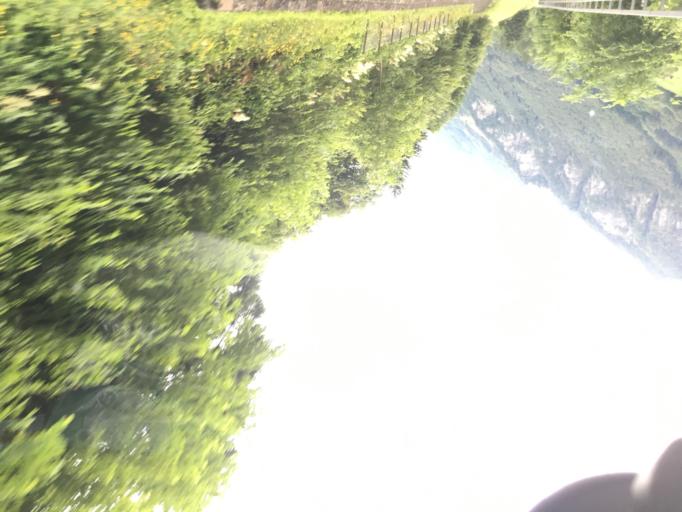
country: CH
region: Obwalden
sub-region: Obwalden
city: Engelberg
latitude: 46.8565
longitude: 8.3720
